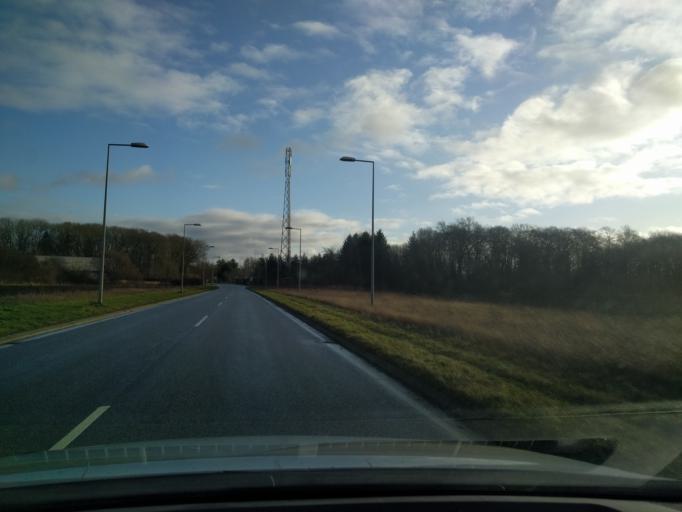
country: DK
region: South Denmark
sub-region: Kerteminde Kommune
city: Langeskov
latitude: 55.3482
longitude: 10.5764
